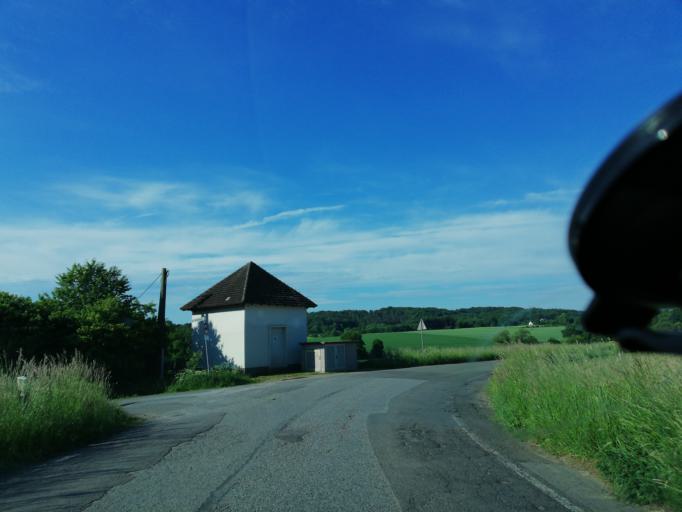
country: DE
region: North Rhine-Westphalia
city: Gevelsberg
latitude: 51.3435
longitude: 7.3250
